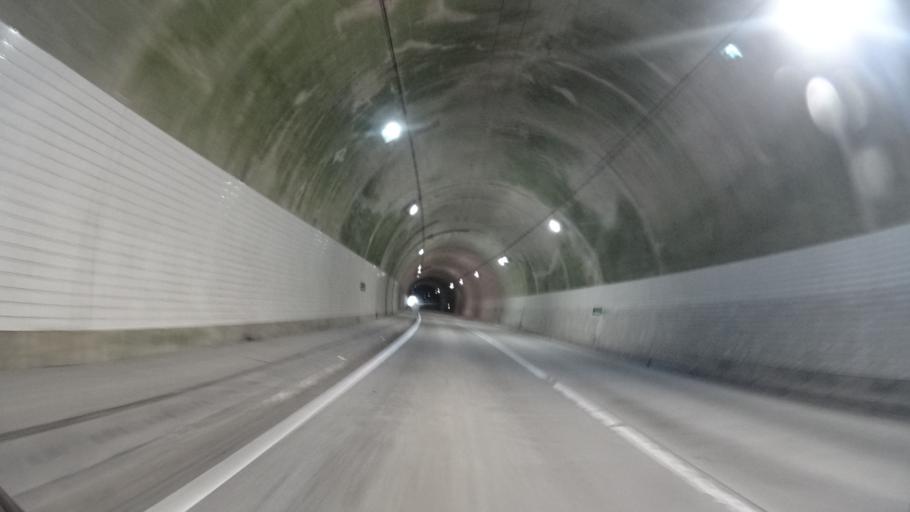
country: JP
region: Ehime
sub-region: Nishiuwa-gun
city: Ikata-cho
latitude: 33.4251
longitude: 132.2092
